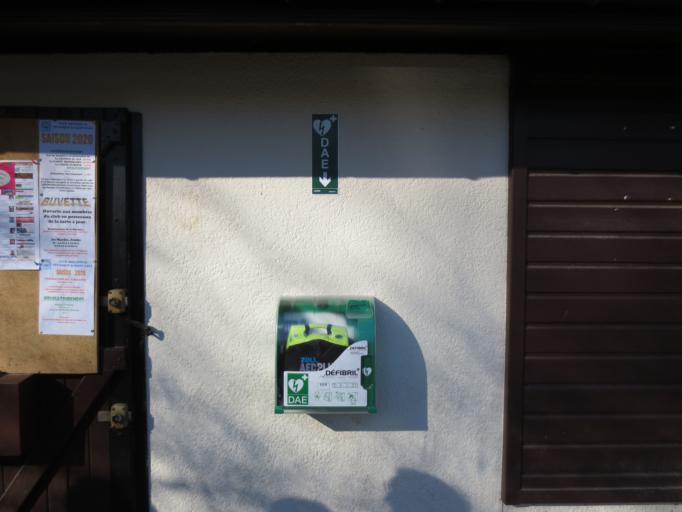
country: FR
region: Aquitaine
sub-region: Departement des Landes
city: Saint-Paul-les-Dax
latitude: 43.7324
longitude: -1.0726
